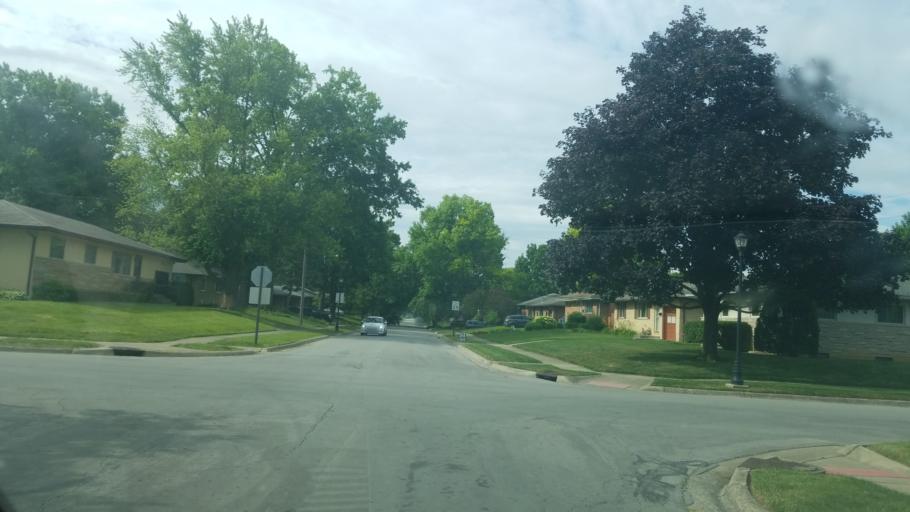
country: US
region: Ohio
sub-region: Franklin County
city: Worthington
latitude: 40.0577
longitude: -82.9928
